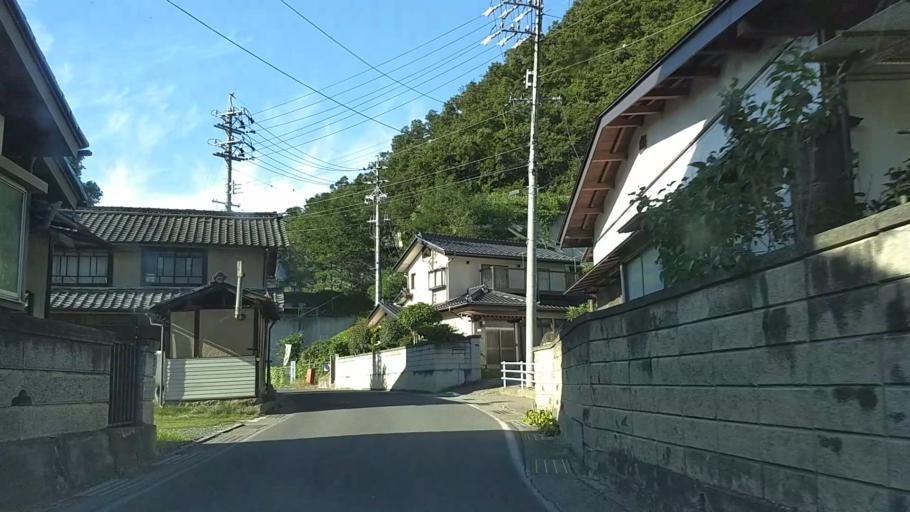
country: JP
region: Nagano
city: Nagano-shi
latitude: 36.5562
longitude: 138.1566
